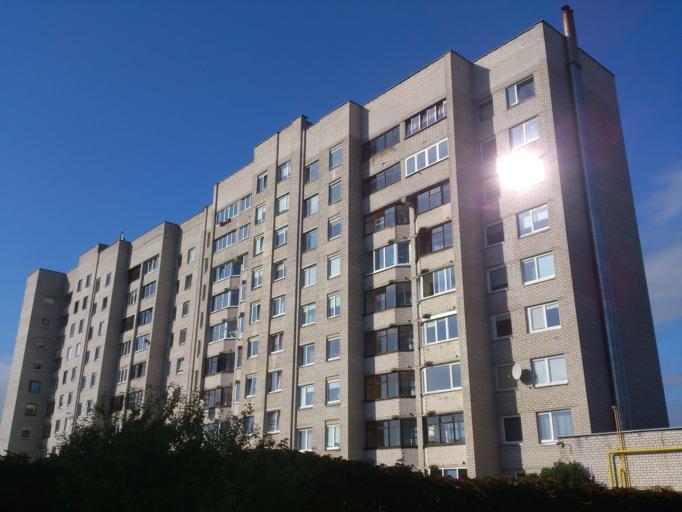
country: LT
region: Kauno apskritis
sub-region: Kaunas
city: Aleksotas
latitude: 54.8746
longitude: 23.9062
